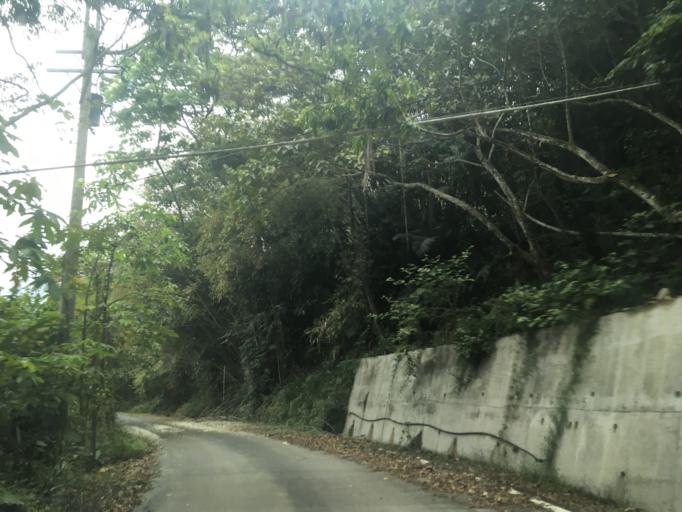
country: TW
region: Taiwan
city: Zhongxing New Village
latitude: 24.0459
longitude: 120.8074
